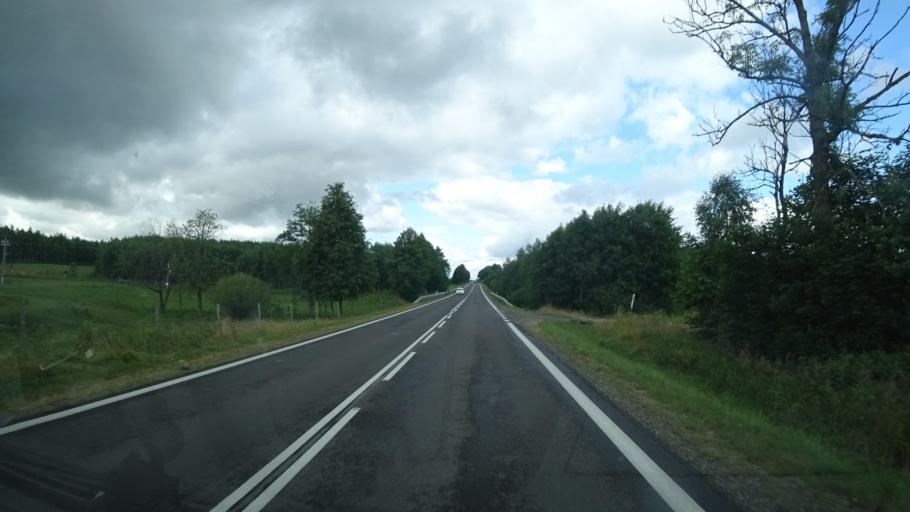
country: PL
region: Warmian-Masurian Voivodeship
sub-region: Powiat goldapski
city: Goldap
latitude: 54.2630
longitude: 22.3559
